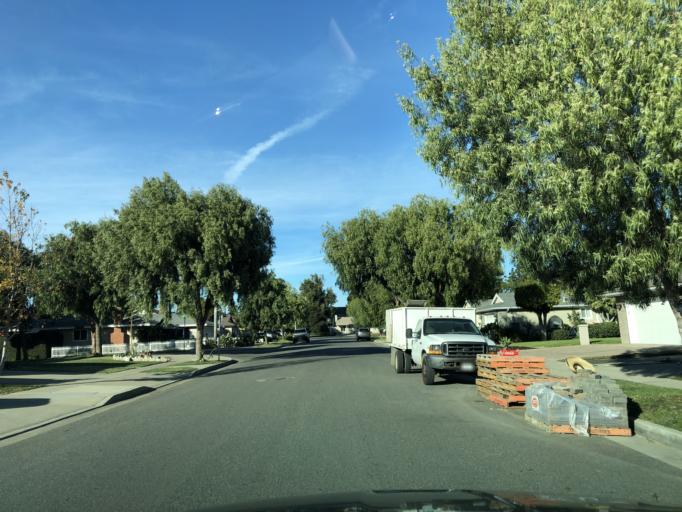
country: US
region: California
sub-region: Orange County
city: Tustin
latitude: 33.7634
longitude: -117.8391
